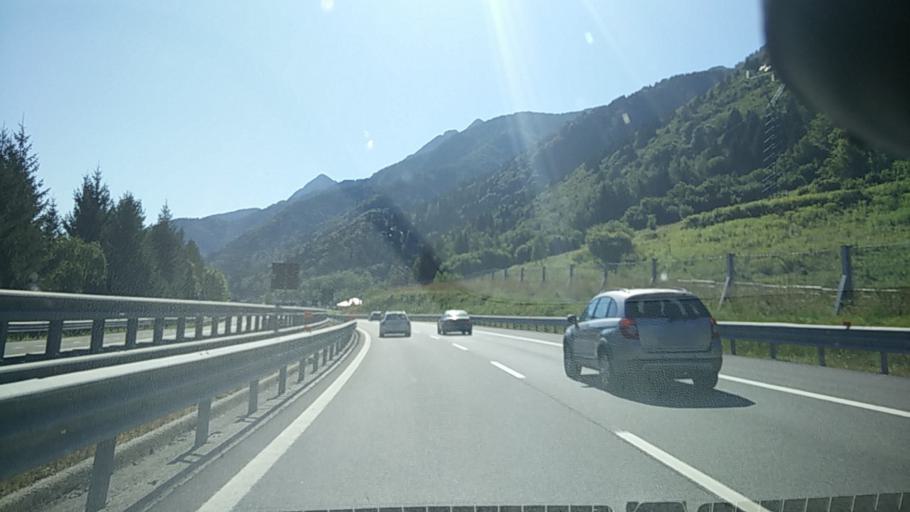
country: IT
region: Friuli Venezia Giulia
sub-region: Provincia di Udine
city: Pontebba
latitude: 46.5006
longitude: 13.3692
